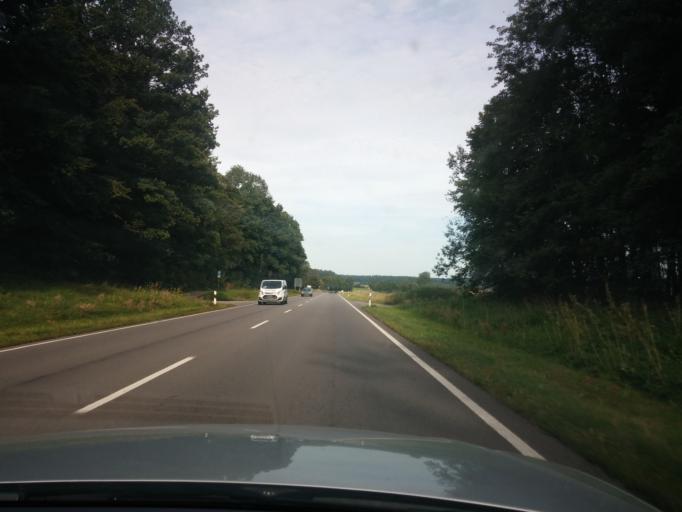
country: DE
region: Baden-Wuerttemberg
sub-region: Tuebingen Region
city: Seekirch
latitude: 48.1223
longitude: 9.6619
